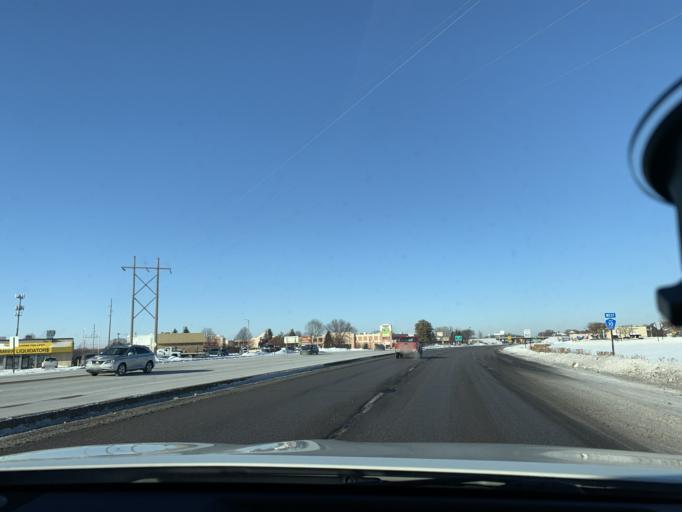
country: US
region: Minnesota
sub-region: Anoka County
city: Coon Rapids
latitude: 45.1317
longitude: -93.2645
